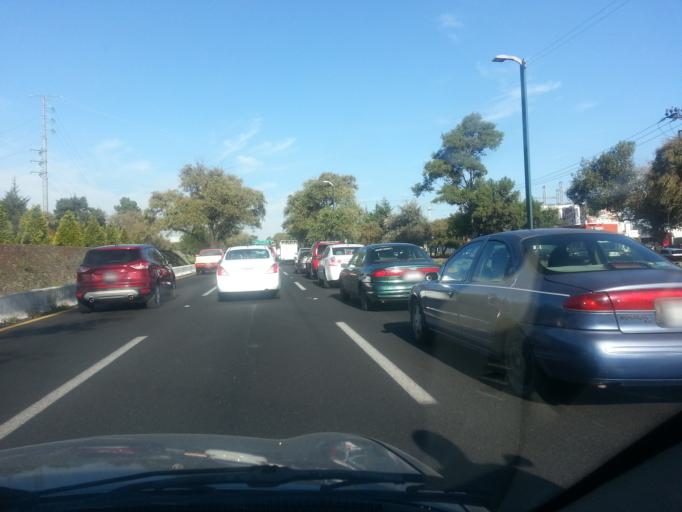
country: MX
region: Mexico
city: Santa Maria Totoltepec
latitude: 19.2876
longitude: -99.5983
